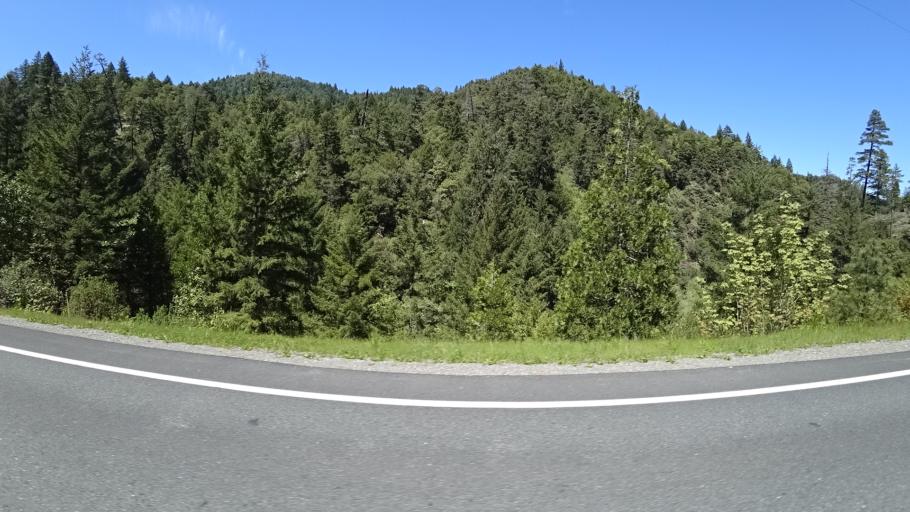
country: US
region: California
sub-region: Humboldt County
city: Willow Creek
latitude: 40.9323
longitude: -123.6791
